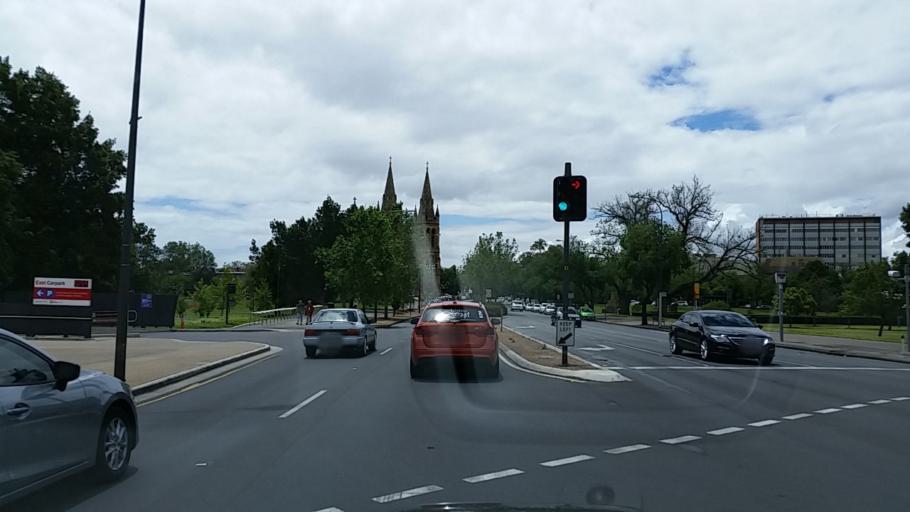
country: AU
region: South Australia
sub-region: Adelaide
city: North Adelaide
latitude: -34.9155
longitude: 138.5988
